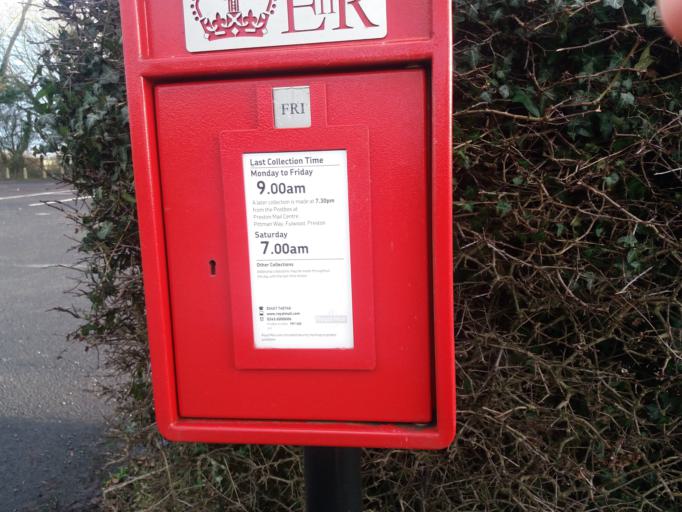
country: GB
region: England
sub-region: Lancashire
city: Euxton
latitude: 53.6708
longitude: -2.7014
